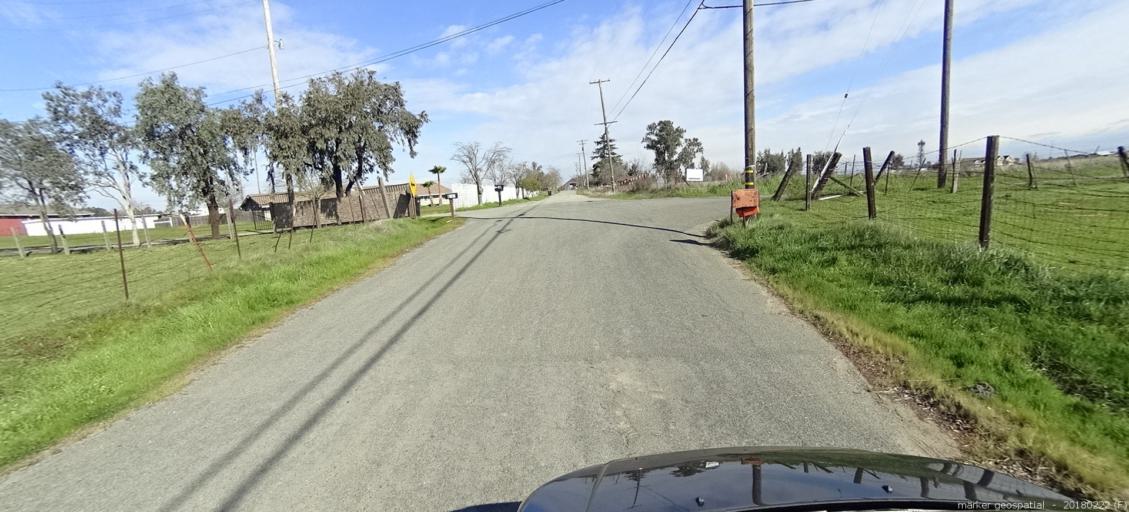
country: US
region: California
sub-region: Sacramento County
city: Elverta
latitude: 38.7252
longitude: -121.4435
